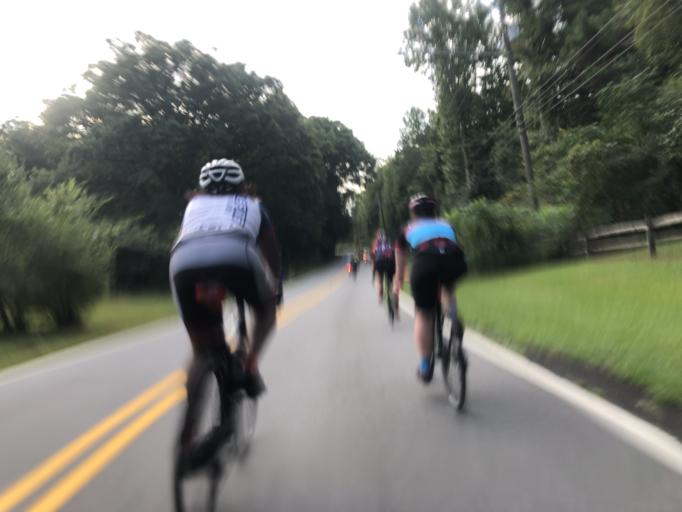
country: US
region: Georgia
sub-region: Fulton County
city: Fairburn
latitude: 33.6029
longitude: -84.6552
